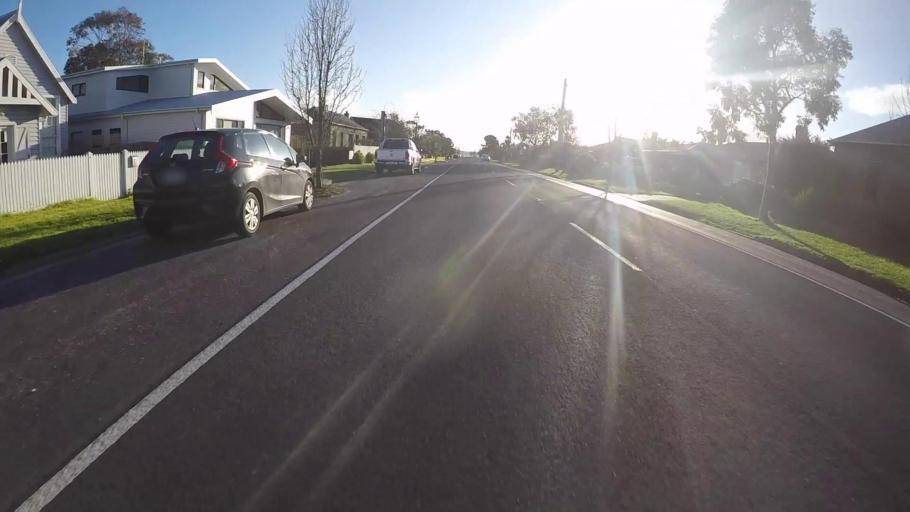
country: AU
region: Victoria
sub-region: Greater Geelong
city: Wandana Heights
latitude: -38.1709
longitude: 144.2758
